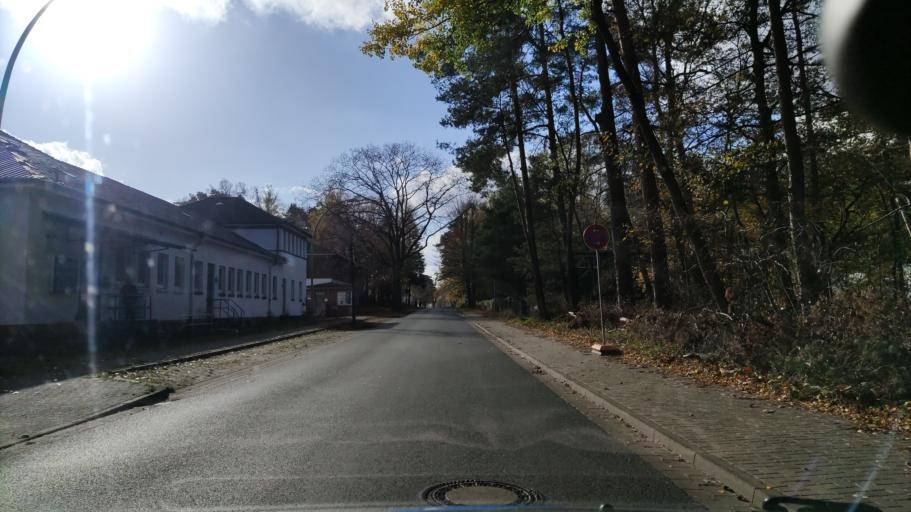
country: DE
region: Lower Saxony
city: Munster
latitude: 53.0023
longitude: 10.1180
